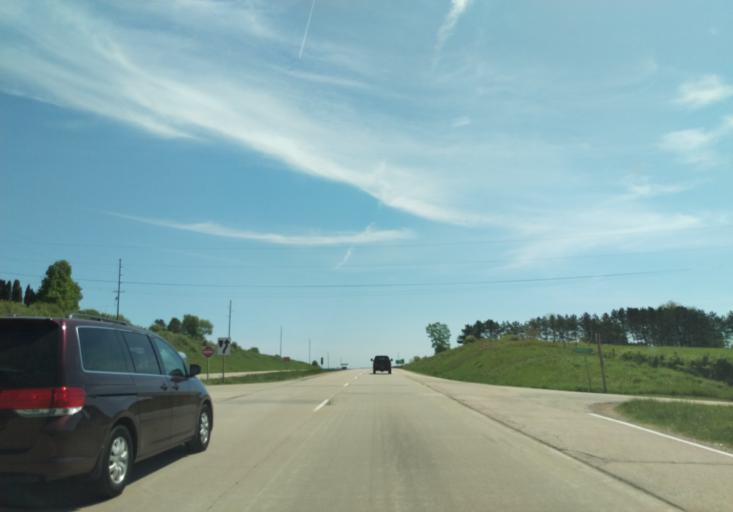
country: US
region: Wisconsin
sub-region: Dane County
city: Verona
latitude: 42.9884
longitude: -89.6157
